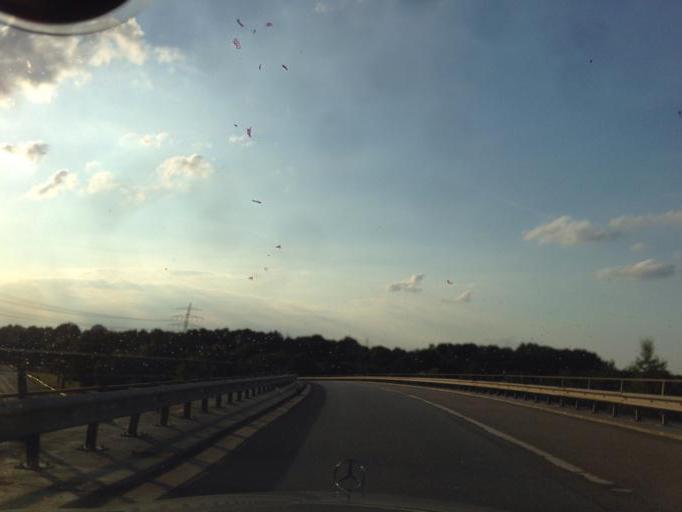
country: DE
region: Schleswig-Holstein
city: Barsbuettel
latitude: 53.5619
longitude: 10.1562
